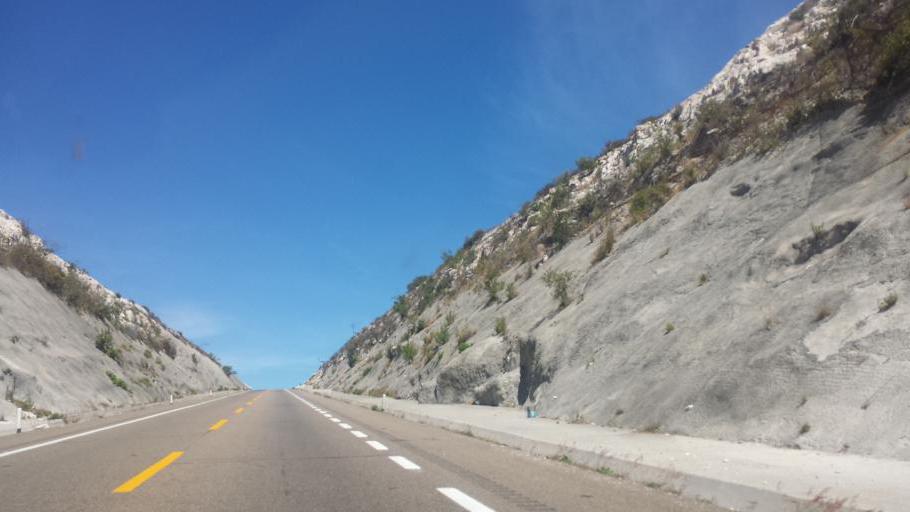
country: MX
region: Oaxaca
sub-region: Villa Tejupam de la Union
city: Villa Tejupam de la Union
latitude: 17.9117
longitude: -97.3634
